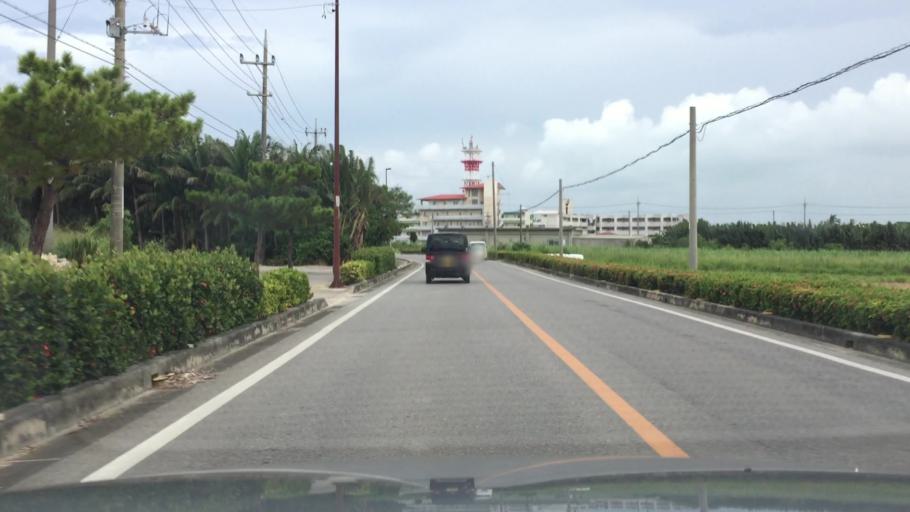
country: JP
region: Okinawa
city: Ishigaki
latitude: 24.3539
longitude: 124.1578
